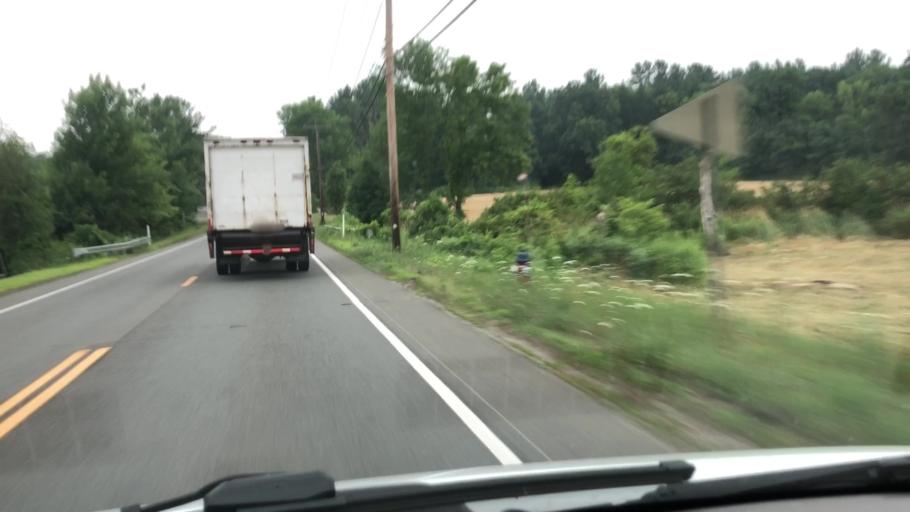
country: US
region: Massachusetts
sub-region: Hampshire County
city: Northampton
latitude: 42.3510
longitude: -72.6904
